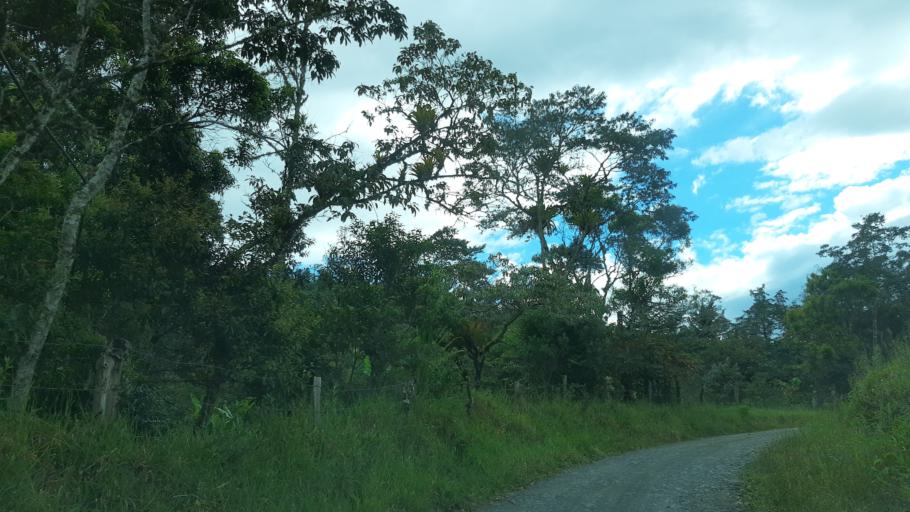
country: CO
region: Boyaca
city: Garagoa
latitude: 5.0192
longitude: -73.3325
